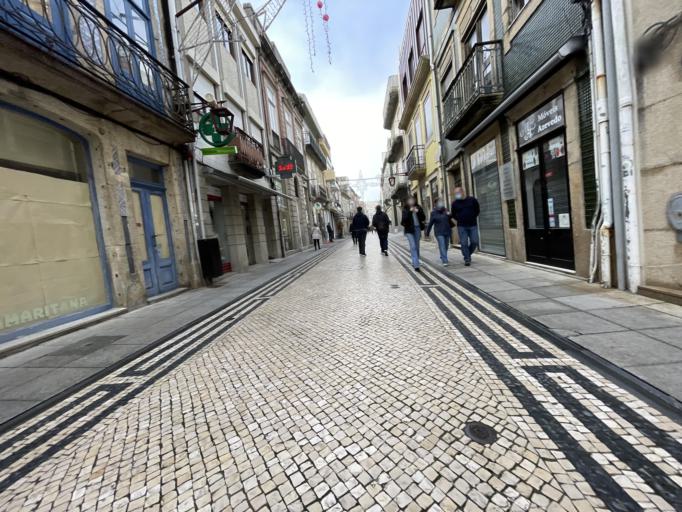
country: PT
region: Porto
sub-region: Povoa de Varzim
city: Povoa de Varzim
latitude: 41.3789
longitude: -8.7628
